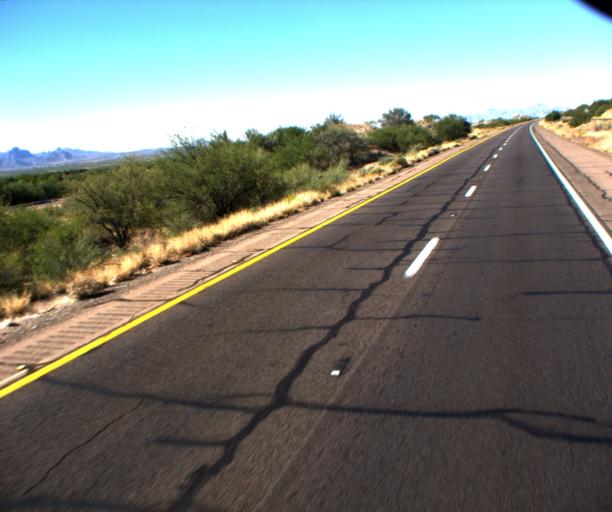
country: US
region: Arizona
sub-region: Pima County
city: Green Valley
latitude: 31.8227
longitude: -111.0048
